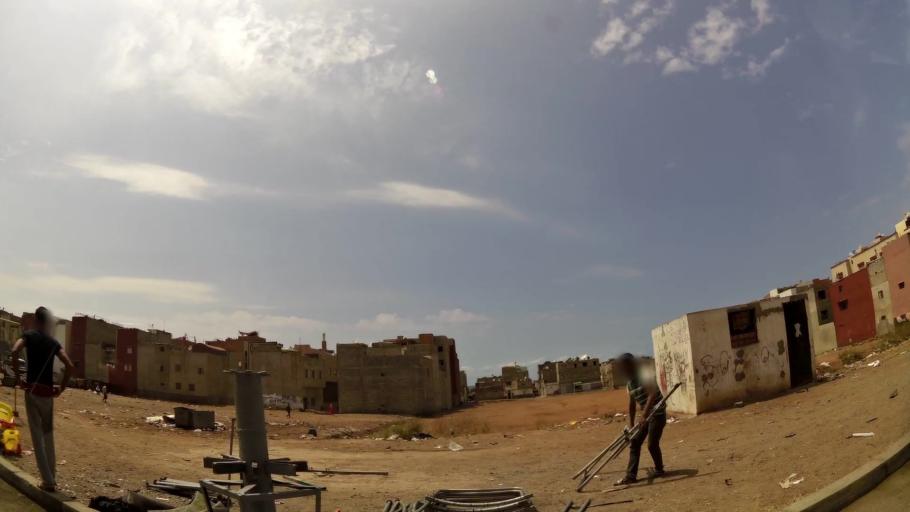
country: MA
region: Rabat-Sale-Zemmour-Zaer
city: Sale
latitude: 34.0553
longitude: -6.8168
